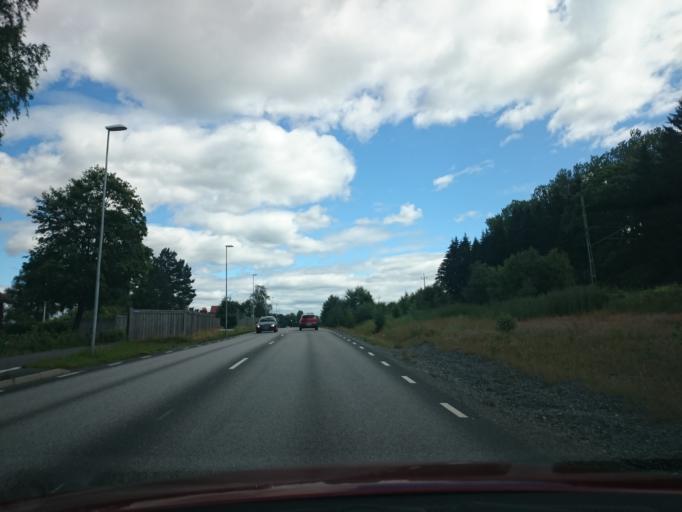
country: SE
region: Vaestra Goetaland
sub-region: Lerums Kommun
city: Lerum
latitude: 57.7799
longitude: 12.2918
